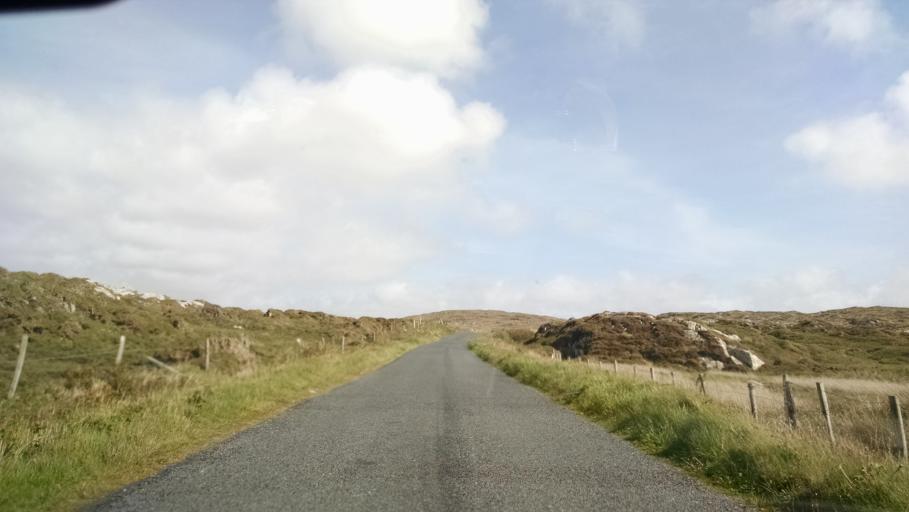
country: IE
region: Connaught
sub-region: County Galway
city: Clifden
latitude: 53.5065
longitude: -10.1094
